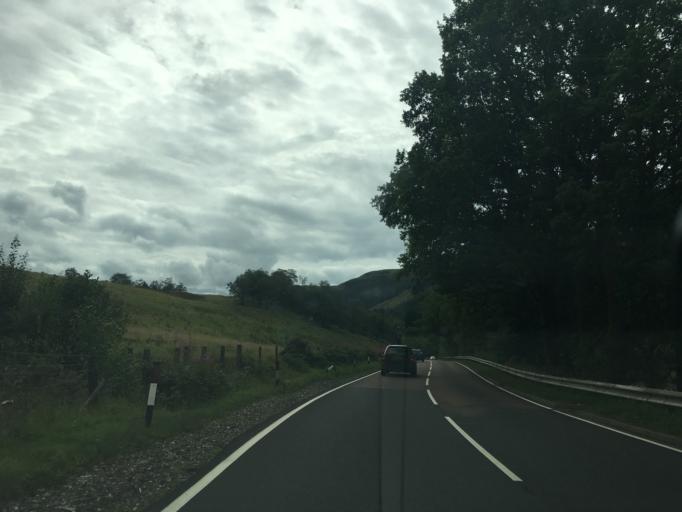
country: GB
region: Scotland
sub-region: Stirling
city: Callander
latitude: 56.2670
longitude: -4.2847
